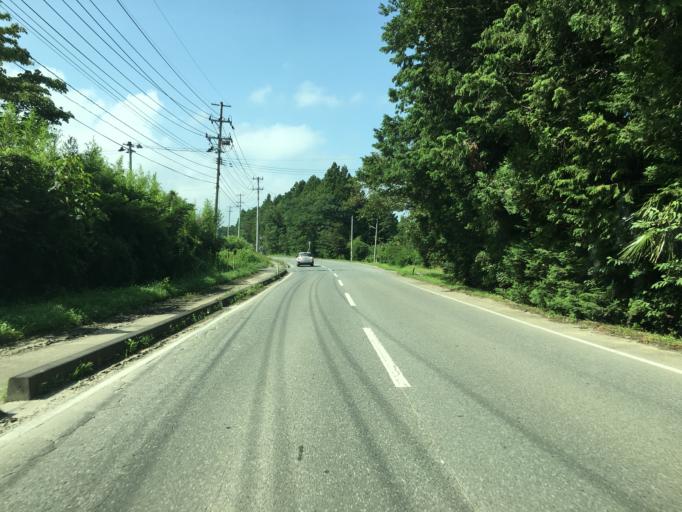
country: JP
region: Miyagi
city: Marumori
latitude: 37.8555
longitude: 140.8959
